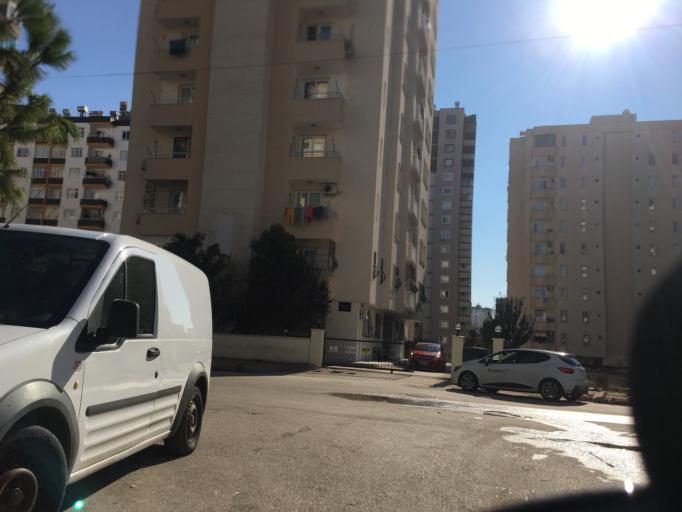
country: TR
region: Adana
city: Seyhan
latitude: 37.0268
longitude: 35.2852
